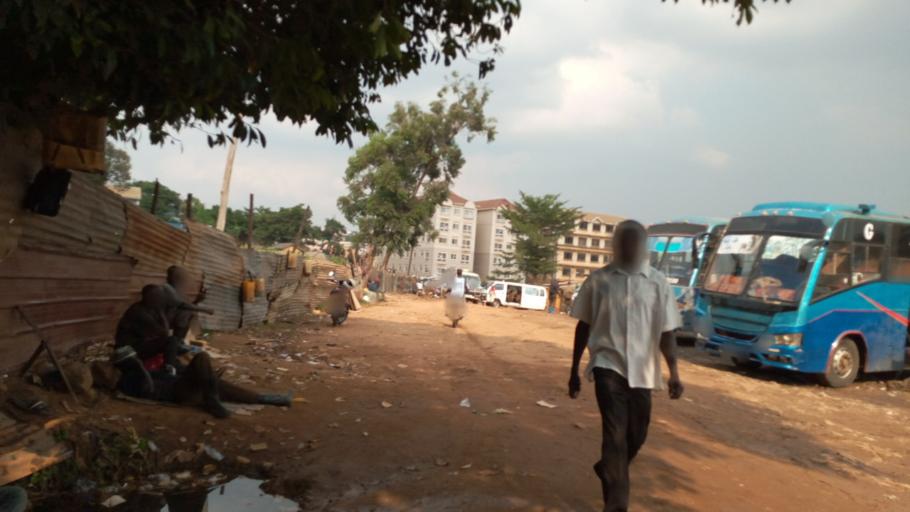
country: UG
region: Central Region
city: Kampala Central Division
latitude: 0.3234
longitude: 32.5686
